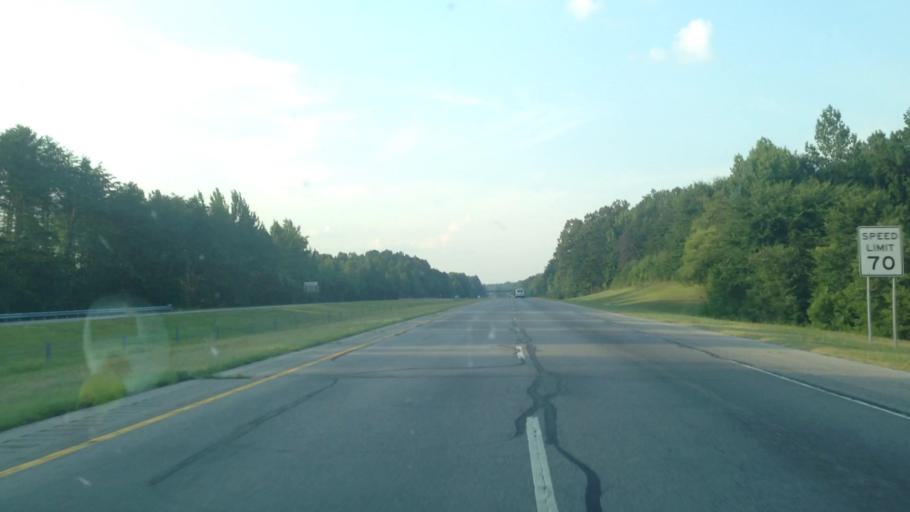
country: US
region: Virginia
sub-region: City of Danville
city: Danville
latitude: 36.4951
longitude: -79.4840
